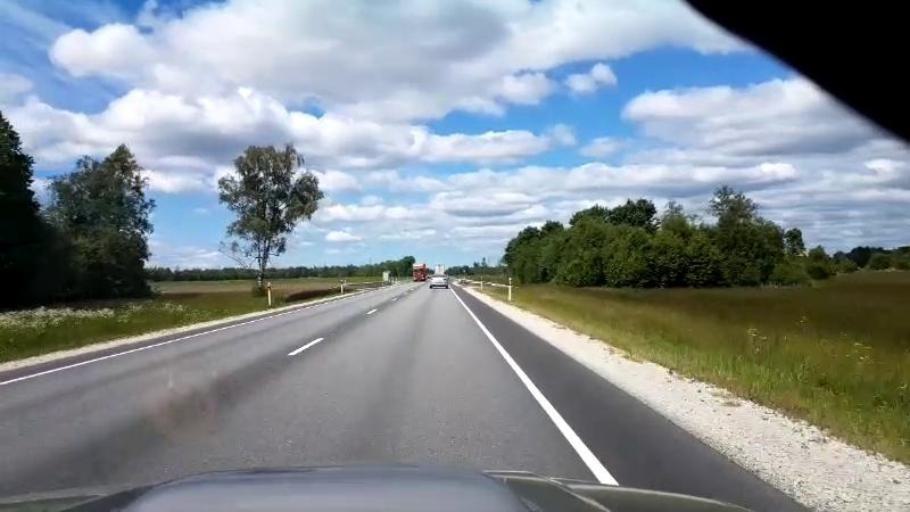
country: EE
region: Paernumaa
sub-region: Halinga vald
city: Parnu-Jaagupi
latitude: 58.6404
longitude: 24.4912
